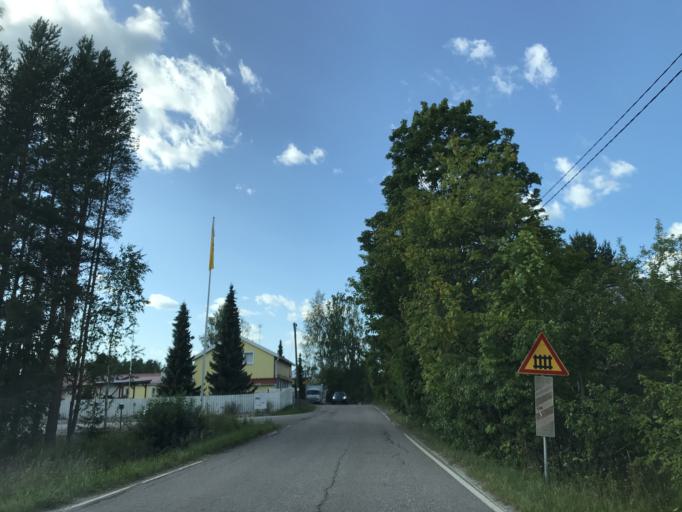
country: FI
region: Uusimaa
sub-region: Helsinki
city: Vihti
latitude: 60.4327
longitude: 24.5209
